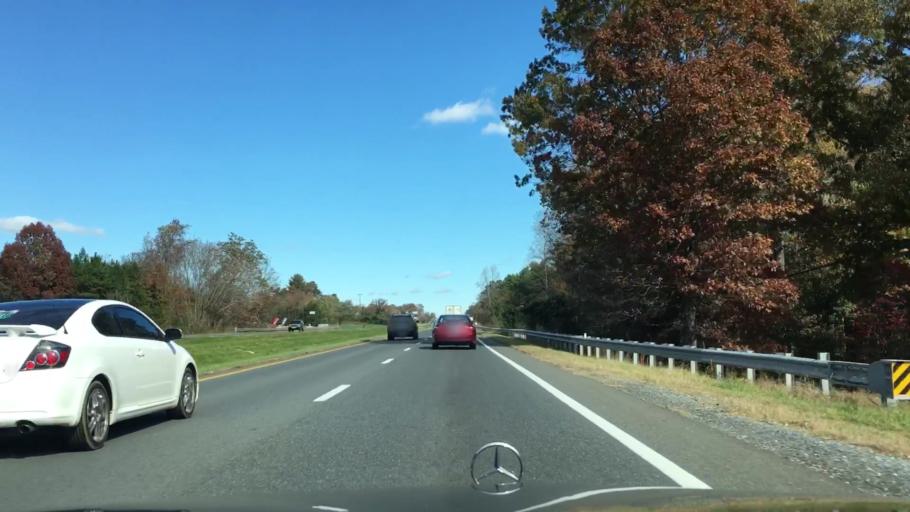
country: US
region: Virginia
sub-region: Campbell County
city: Rustburg
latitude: 37.2670
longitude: -79.1771
